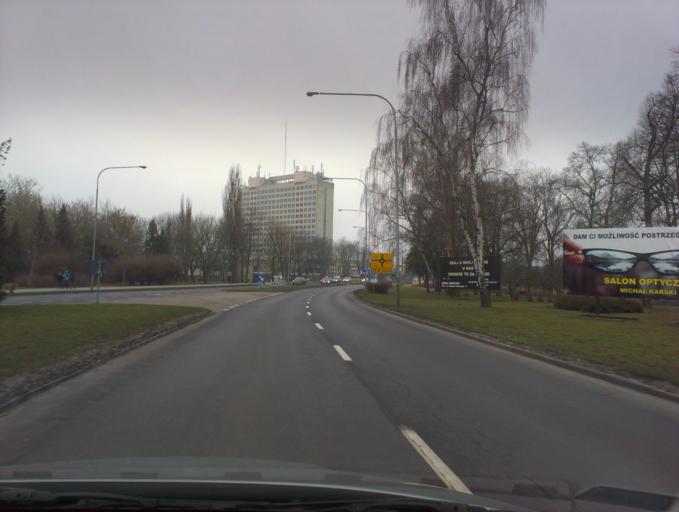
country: PL
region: Greater Poland Voivodeship
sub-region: Powiat pilski
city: Pila
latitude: 53.1522
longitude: 16.7421
